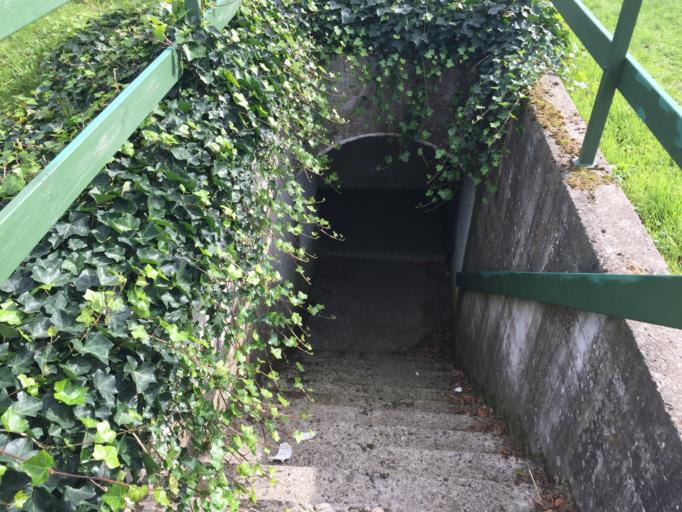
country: DK
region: South Denmark
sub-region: Svendborg Kommune
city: Svendborg
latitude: 55.0702
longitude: 10.5127
